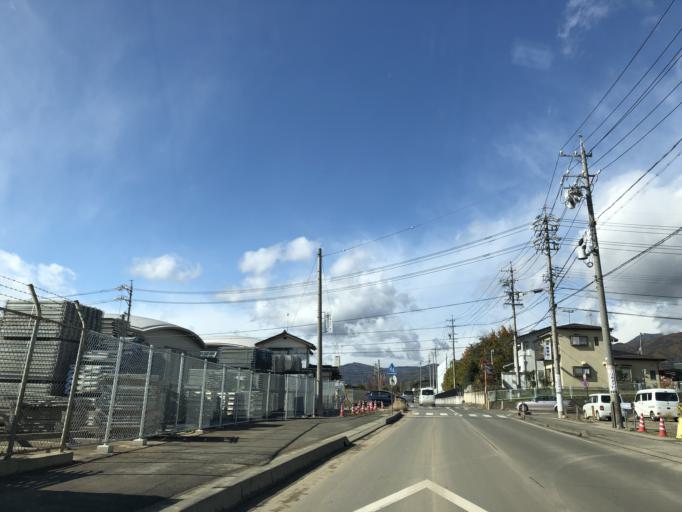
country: JP
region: Nagano
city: Suzaka
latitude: 36.6830
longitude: 138.2593
